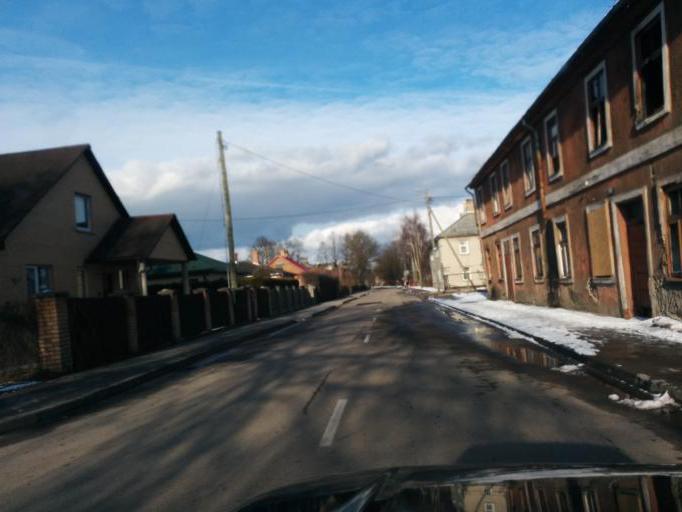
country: LV
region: Jelgava
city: Jelgava
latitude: 56.6545
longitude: 23.7094
